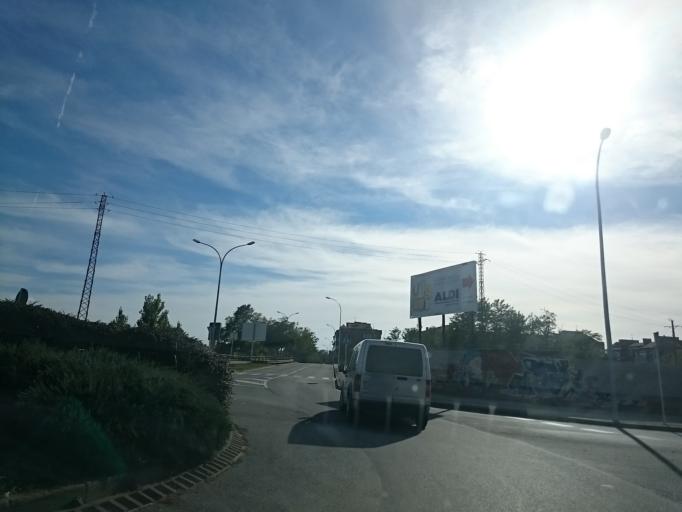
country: ES
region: Catalonia
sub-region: Provincia de Barcelona
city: Vic
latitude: 41.9262
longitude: 2.2642
